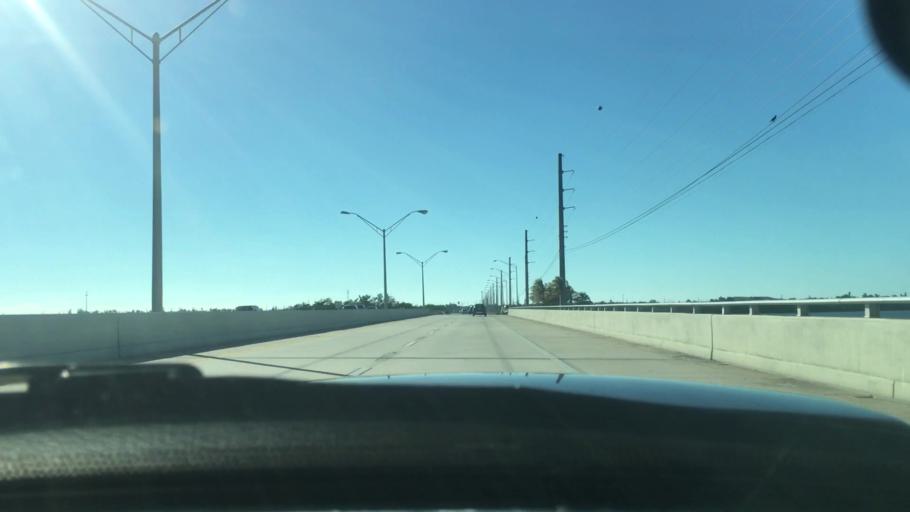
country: US
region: Florida
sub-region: Monroe County
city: Stock Island
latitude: 24.5773
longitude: -81.7195
